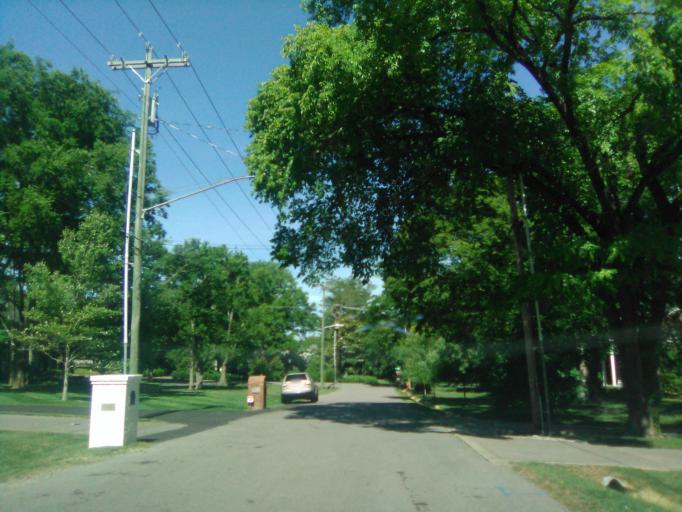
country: US
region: Tennessee
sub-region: Davidson County
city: Belle Meade
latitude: 36.1178
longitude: -86.8297
